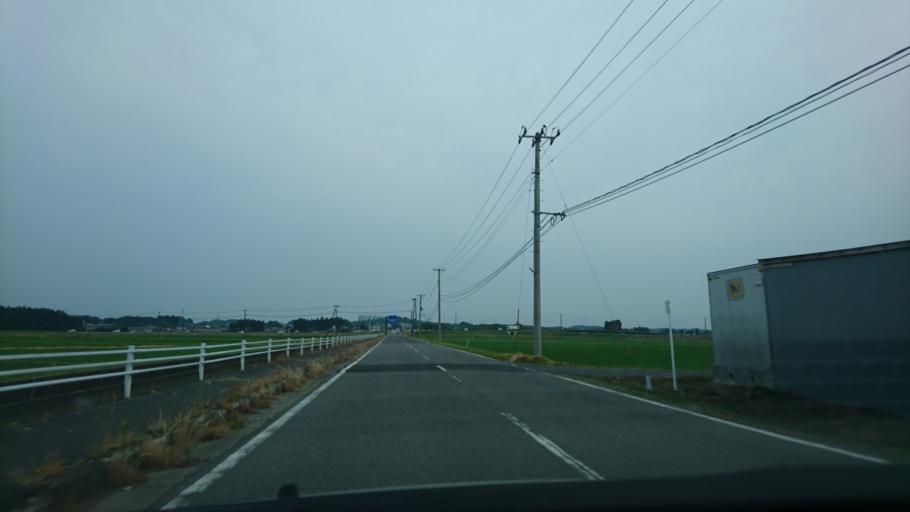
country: JP
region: Iwate
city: Ichinoseki
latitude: 38.7514
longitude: 141.0310
